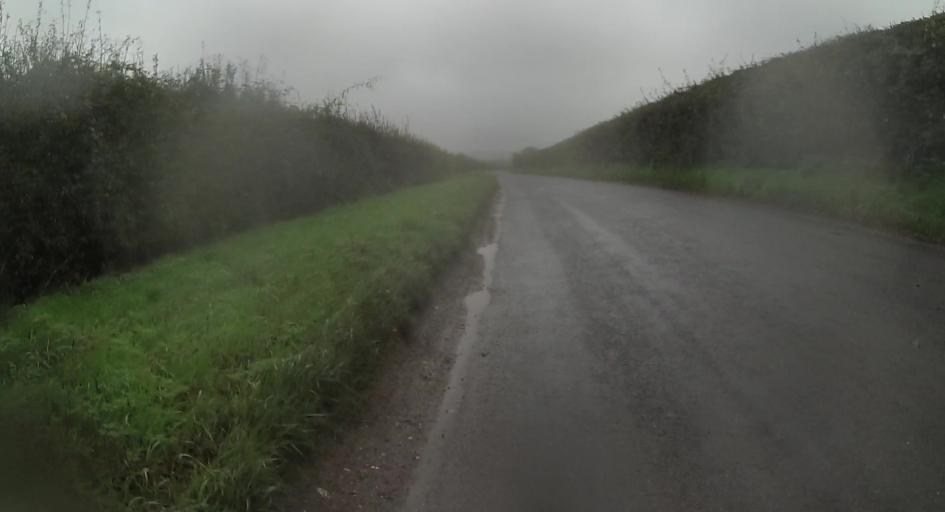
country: GB
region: England
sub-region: Hampshire
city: Four Marks
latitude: 51.1629
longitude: -1.1266
